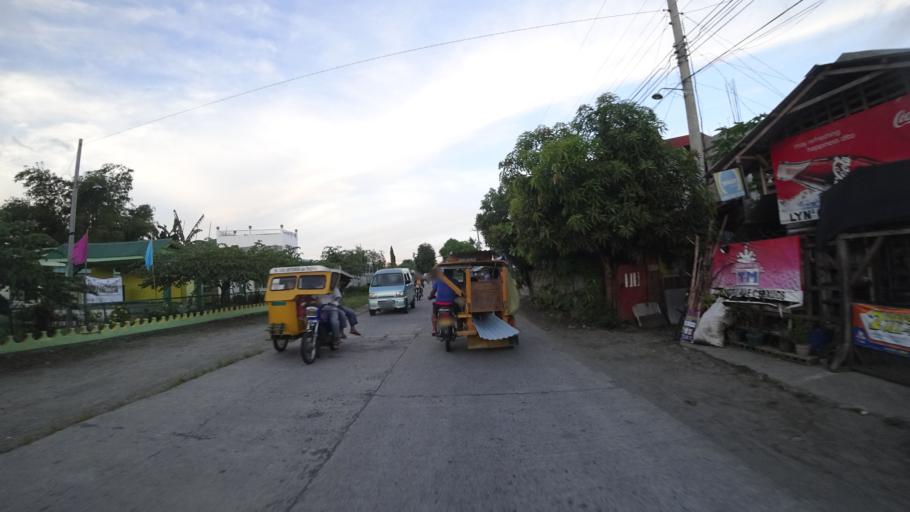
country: PH
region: Eastern Visayas
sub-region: Province of Leyte
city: Pawing
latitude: 11.1644
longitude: 125.0059
